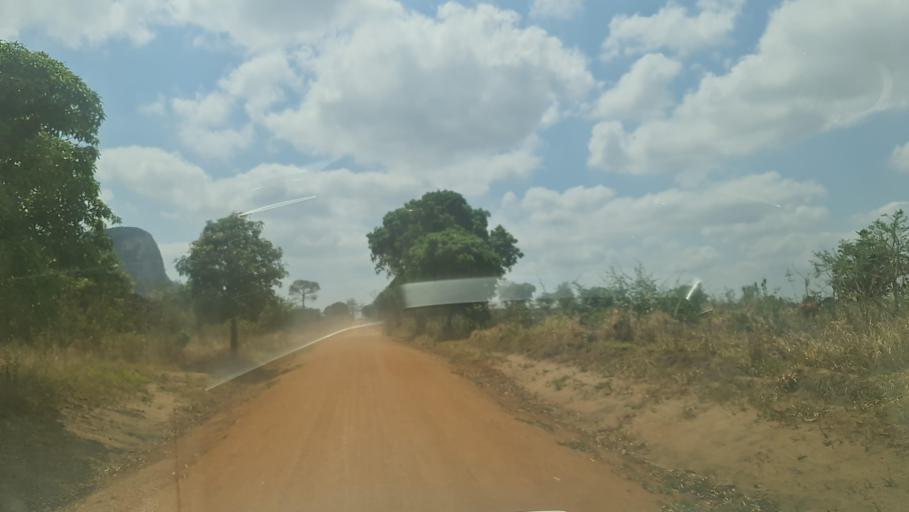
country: MW
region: Southern Region
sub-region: Nsanje District
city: Nsanje
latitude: -17.3953
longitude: 35.5678
